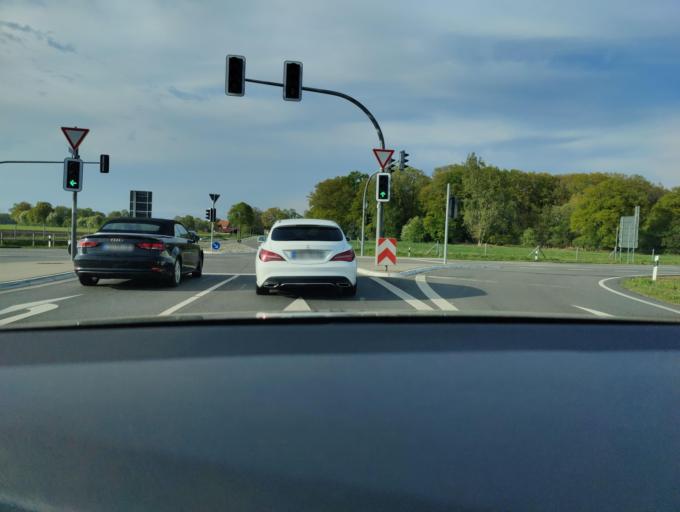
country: DE
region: Lower Saxony
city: Nordhorn
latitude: 52.4565
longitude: 7.0898
